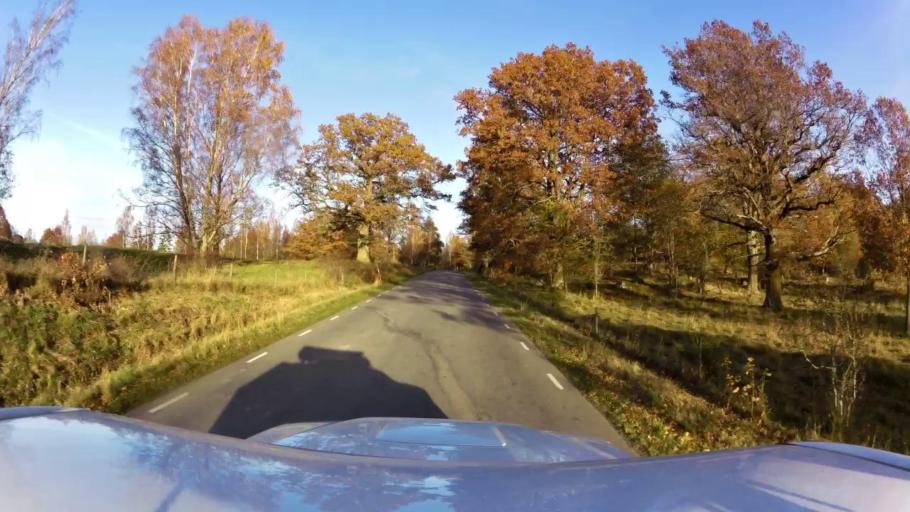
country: SE
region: OEstergoetland
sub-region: Linkopings Kommun
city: Sturefors
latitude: 58.3138
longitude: 15.6739
